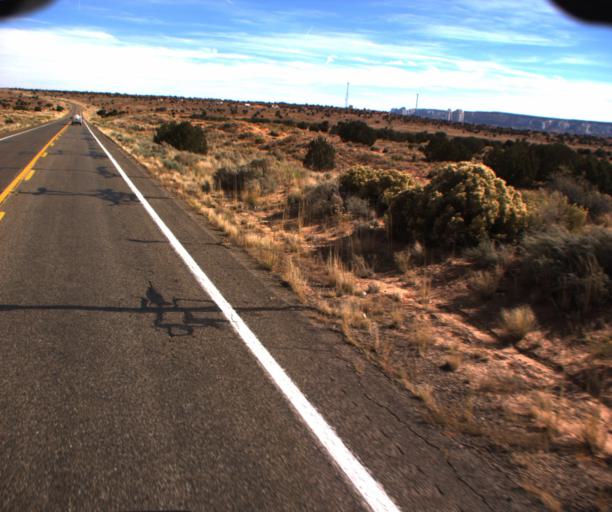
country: US
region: Arizona
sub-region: Coconino County
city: Kaibito
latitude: 36.5775
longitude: -111.1157
